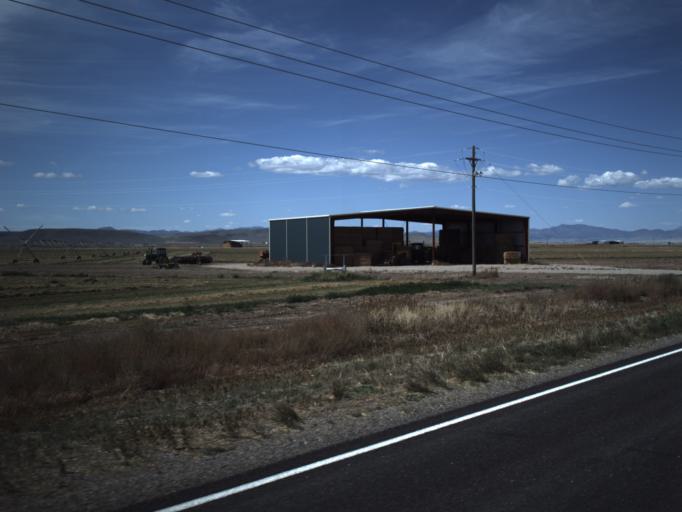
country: US
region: Utah
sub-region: Washington County
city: Enterprise
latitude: 37.6269
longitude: -113.6612
